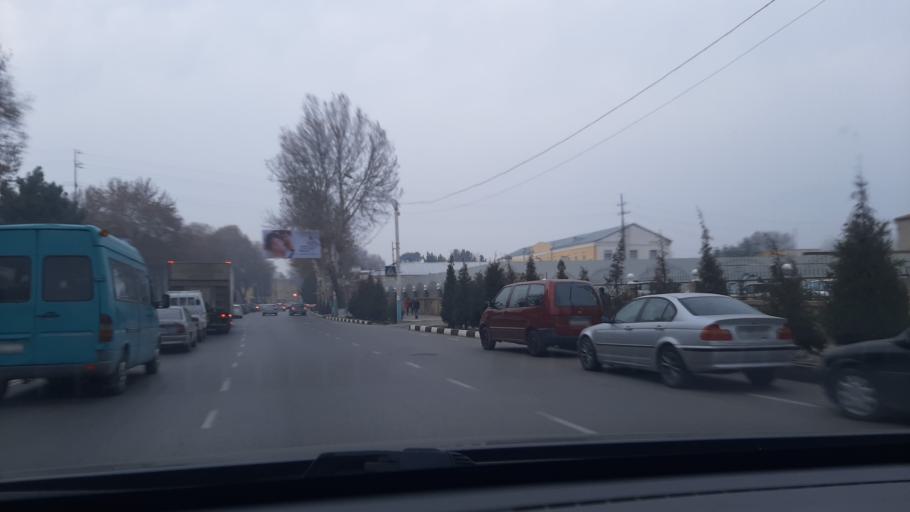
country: TJ
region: Viloyati Sughd
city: Khujand
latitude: 40.2725
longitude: 69.6417
